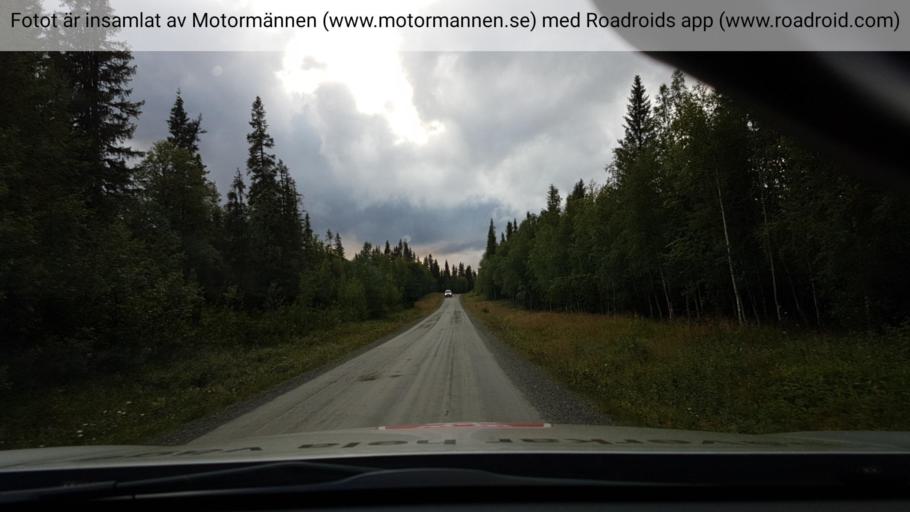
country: SE
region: Vaesterbotten
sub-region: Vilhelmina Kommun
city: Sjoberg
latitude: 65.5067
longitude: 15.6452
